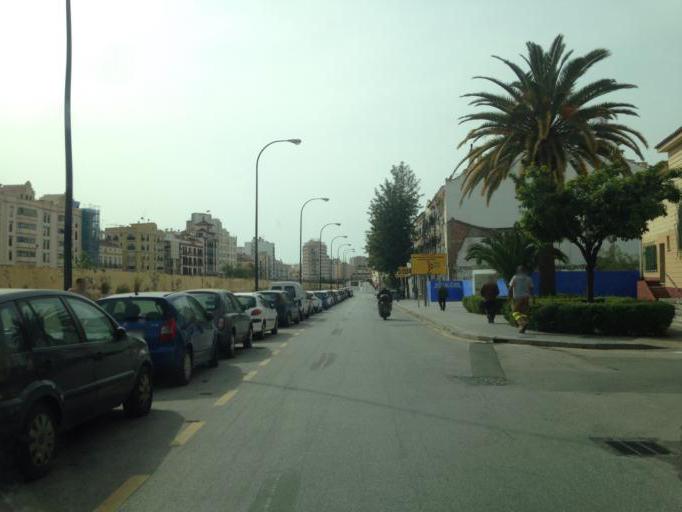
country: ES
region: Andalusia
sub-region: Provincia de Malaga
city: Malaga
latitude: 36.7243
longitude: -4.4263
